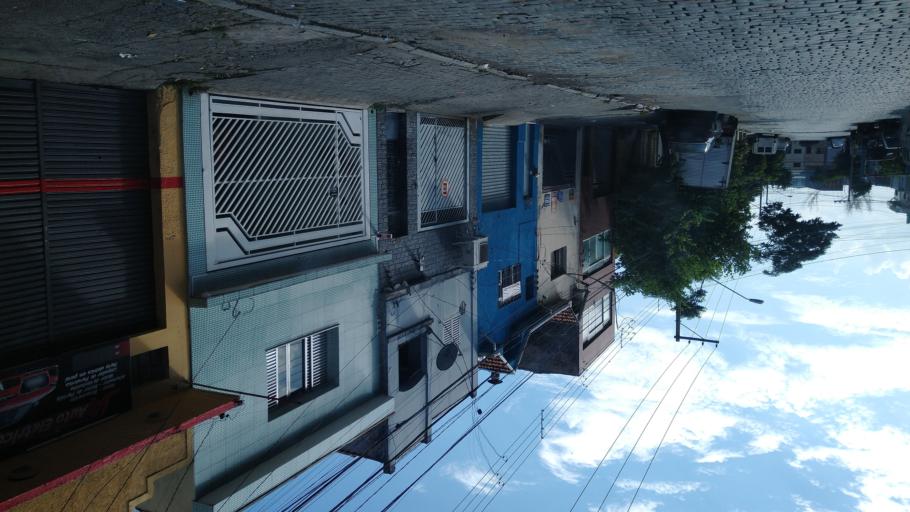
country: BR
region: Sao Paulo
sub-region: Sao Paulo
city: Sao Paulo
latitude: -23.5360
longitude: -46.6032
